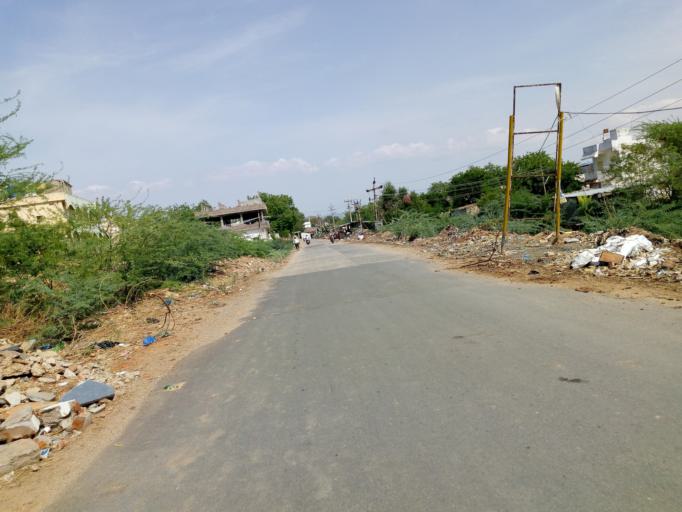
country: IN
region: Andhra Pradesh
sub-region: Prakasam
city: Cumbum
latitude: 15.5845
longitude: 79.1095
